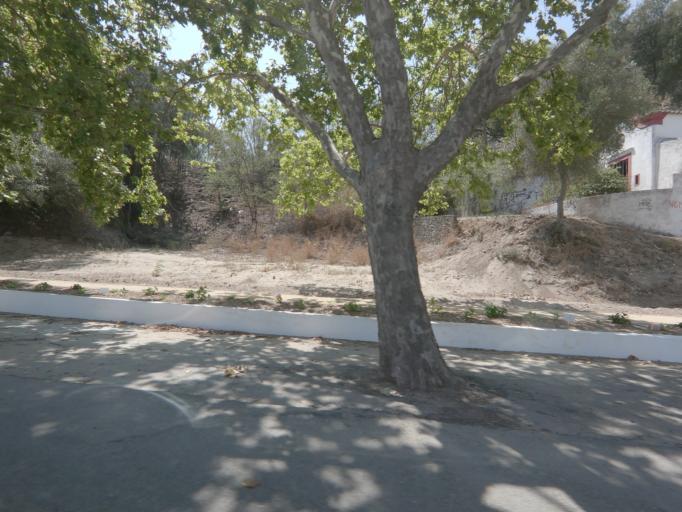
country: PT
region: Setubal
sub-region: Setubal
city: Setubal
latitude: 38.5326
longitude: -8.8999
